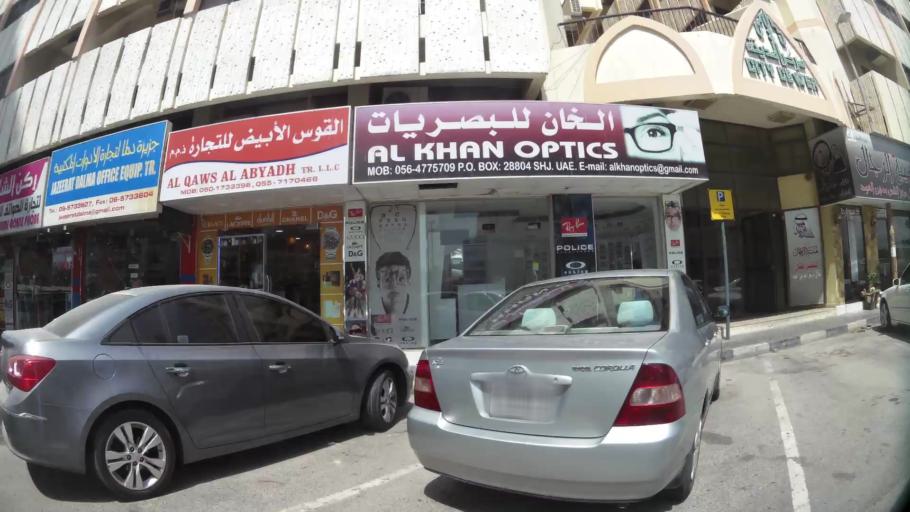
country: AE
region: Ash Shariqah
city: Sharjah
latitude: 25.3408
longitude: 55.3862
